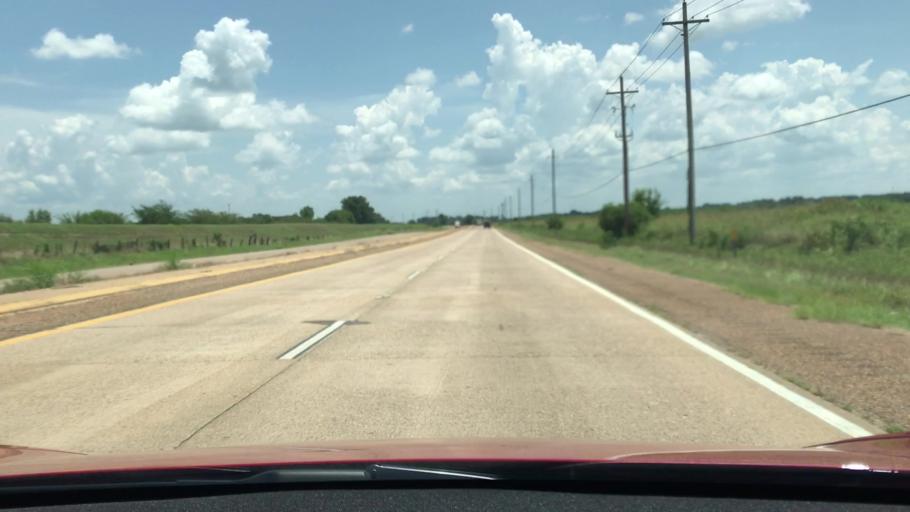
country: US
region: Louisiana
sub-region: Bossier Parish
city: Bossier City
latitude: 32.3943
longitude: -93.6875
